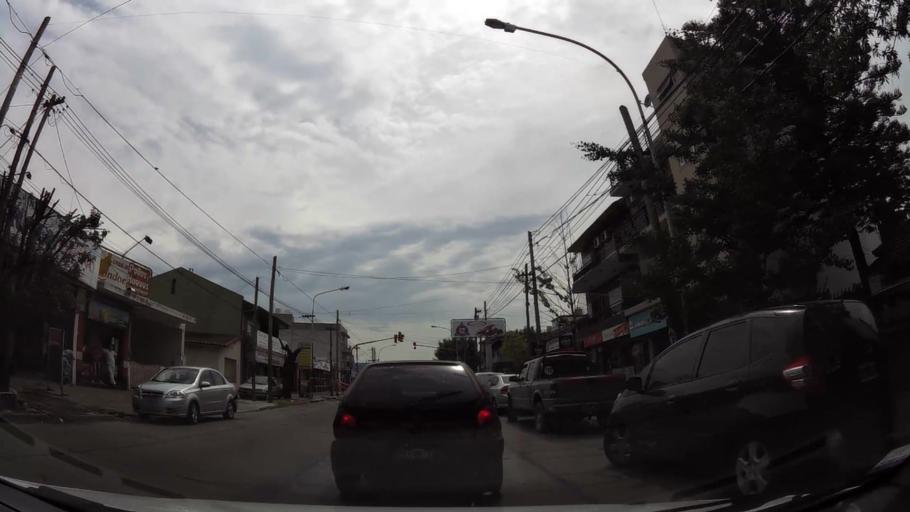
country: AR
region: Buenos Aires F.D.
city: Villa Lugano
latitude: -34.6964
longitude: -58.5050
